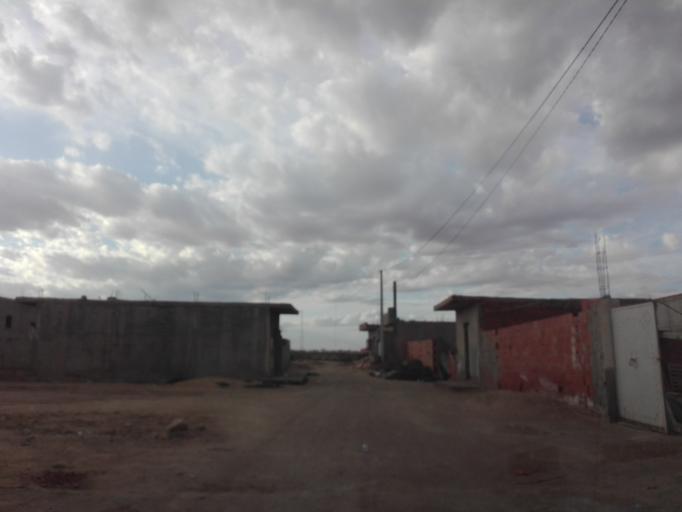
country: TN
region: Safaqis
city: Al Qarmadah
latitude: 34.8075
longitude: 10.8598
